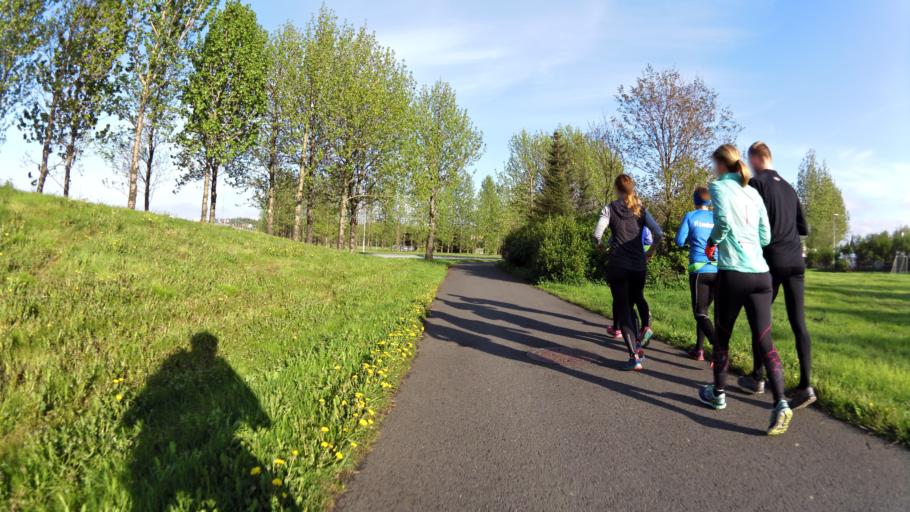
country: IS
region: Capital Region
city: Reykjavik
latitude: 64.1250
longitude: -21.8521
